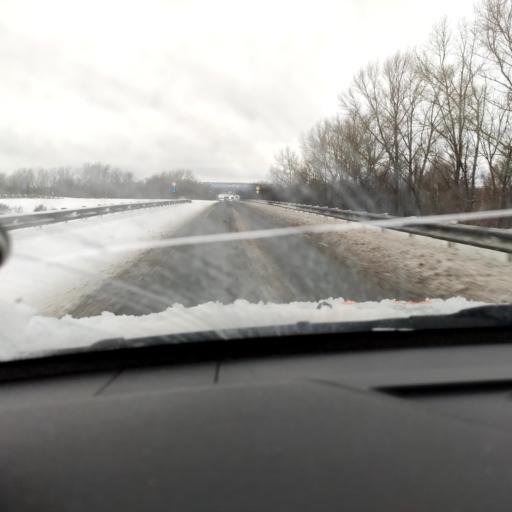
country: RU
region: Samara
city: Novosemeykino
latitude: 53.4177
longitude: 50.3377
